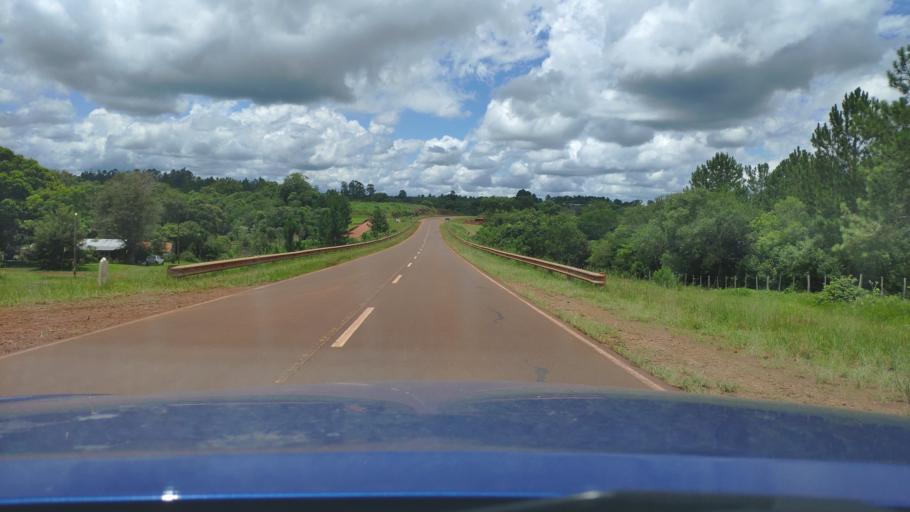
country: AR
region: Misiones
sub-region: Departamento de San Javier
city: San Javier
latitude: -27.8410
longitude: -55.2337
